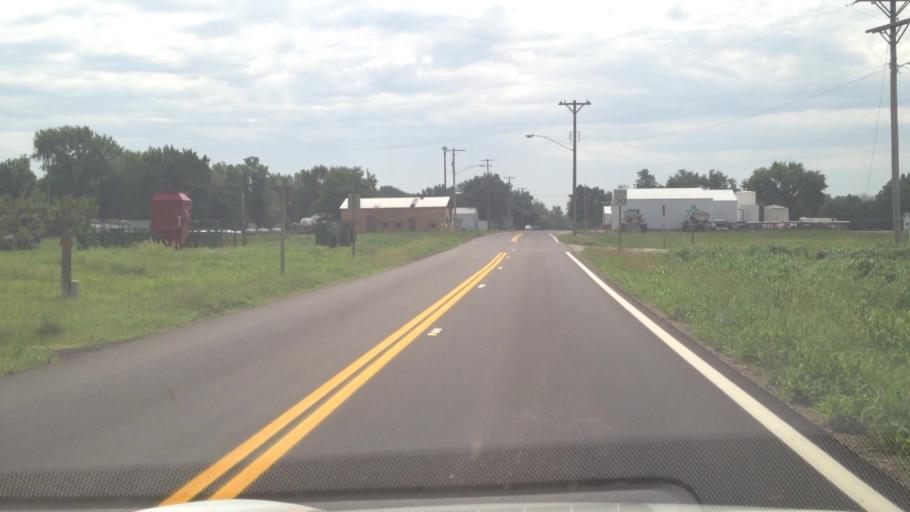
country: US
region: Kansas
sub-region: Crawford County
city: Girard
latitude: 37.6648
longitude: -94.9696
